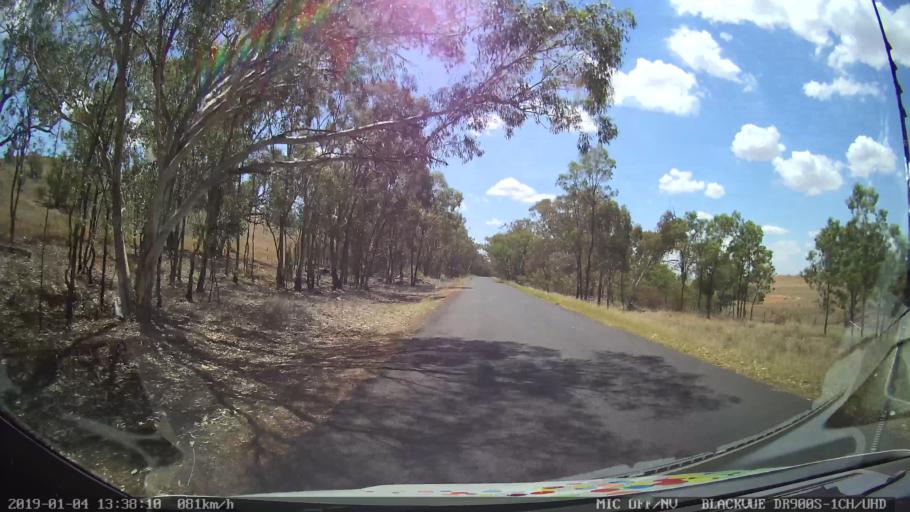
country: AU
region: New South Wales
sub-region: Dubbo Municipality
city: Dubbo
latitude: -32.5413
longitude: 148.5466
